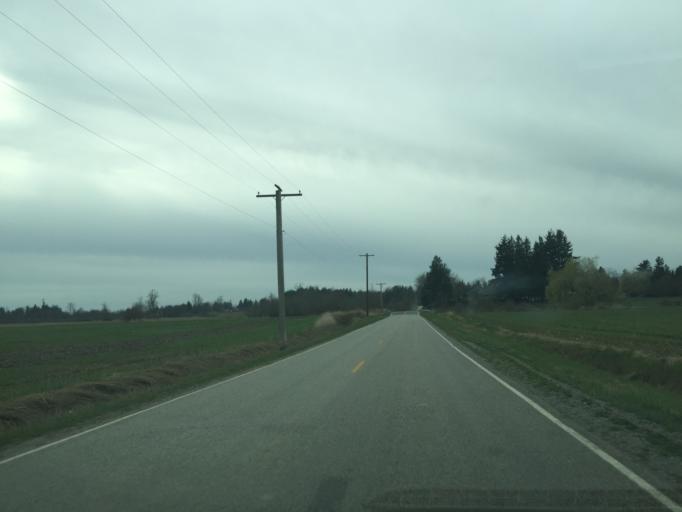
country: US
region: Washington
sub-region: Whatcom County
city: Nooksack
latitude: 48.9784
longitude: -122.3160
